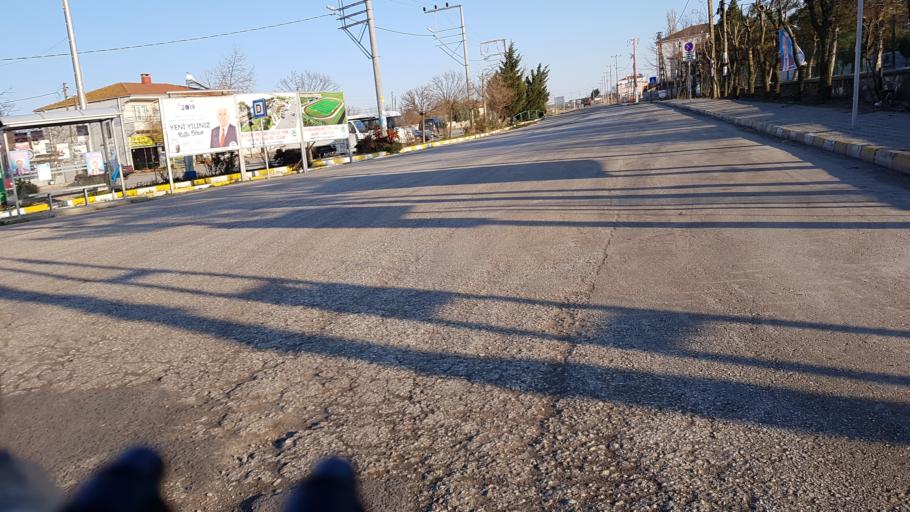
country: TR
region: Tekirdag
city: Beyazkoy
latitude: 41.3053
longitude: 27.7884
